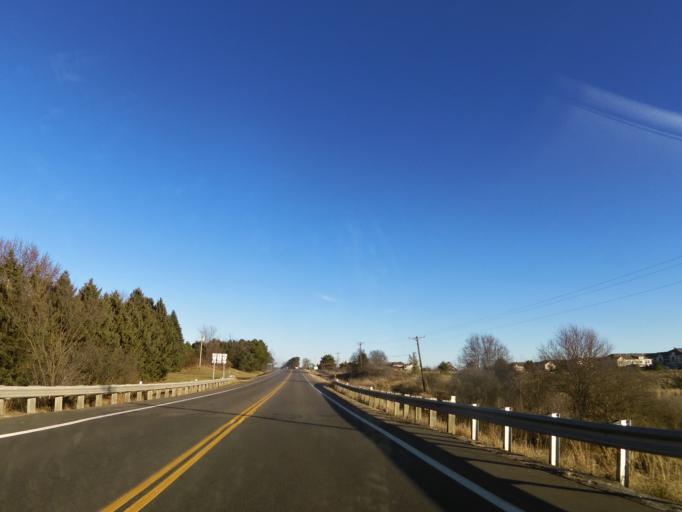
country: US
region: Minnesota
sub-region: Washington County
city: Grant
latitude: 45.0795
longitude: -92.8609
